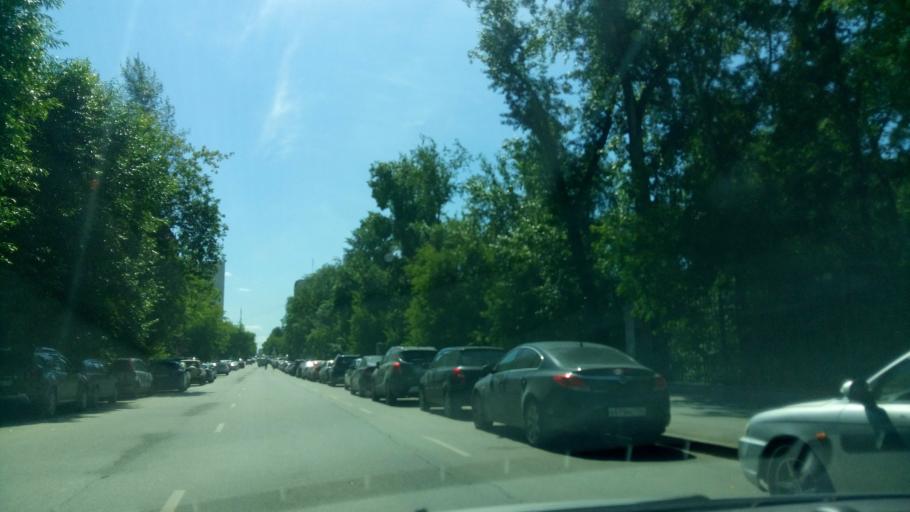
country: RU
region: Sverdlovsk
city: Yekaterinburg
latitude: 56.8482
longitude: 60.6149
